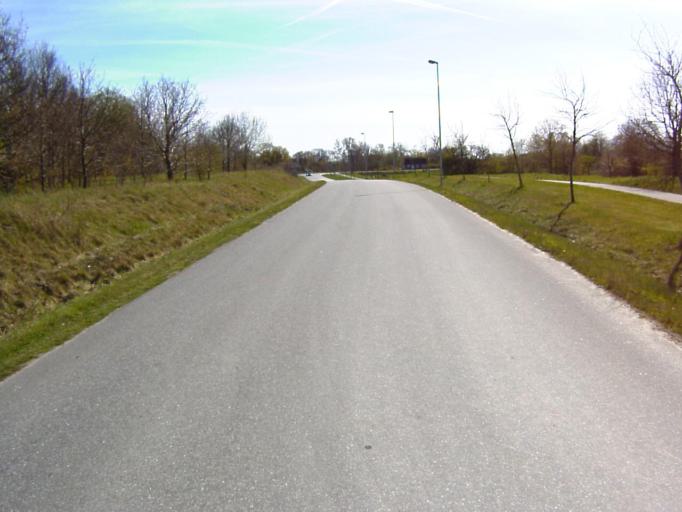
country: SE
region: Skane
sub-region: Kristianstads Kommun
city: Onnestad
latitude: 55.9970
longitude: 14.0661
